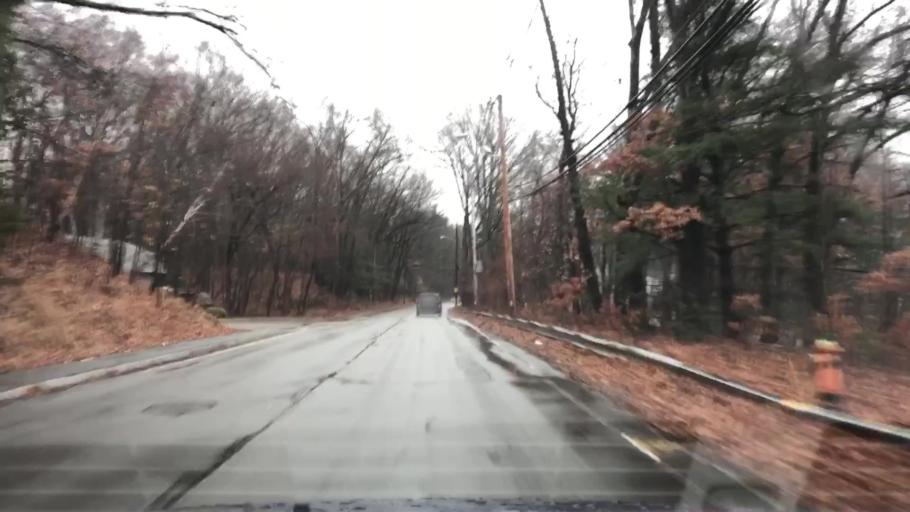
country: US
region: Massachusetts
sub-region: Essex County
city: North Andover
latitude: 42.6846
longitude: -71.1340
